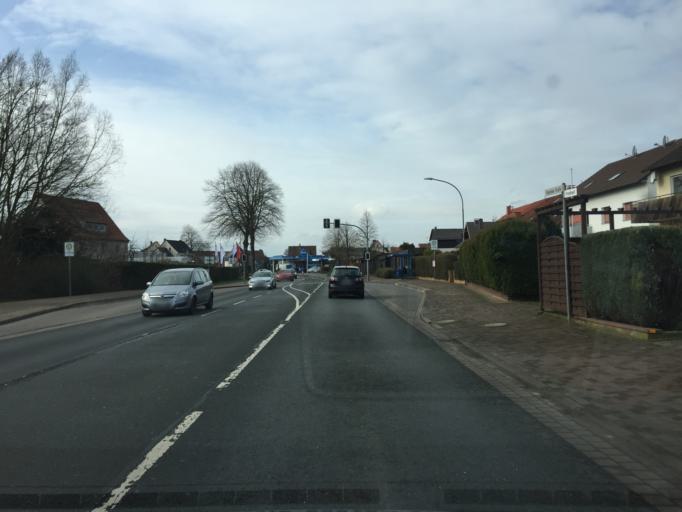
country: DE
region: Lower Saxony
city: Aerzen
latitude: 52.0706
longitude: 9.3108
